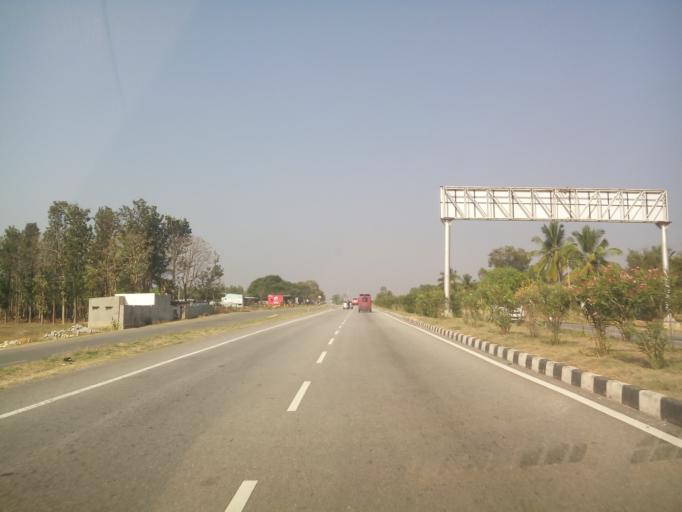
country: IN
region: Karnataka
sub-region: Tumkur
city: Kunigal
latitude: 13.0023
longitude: 76.9498
